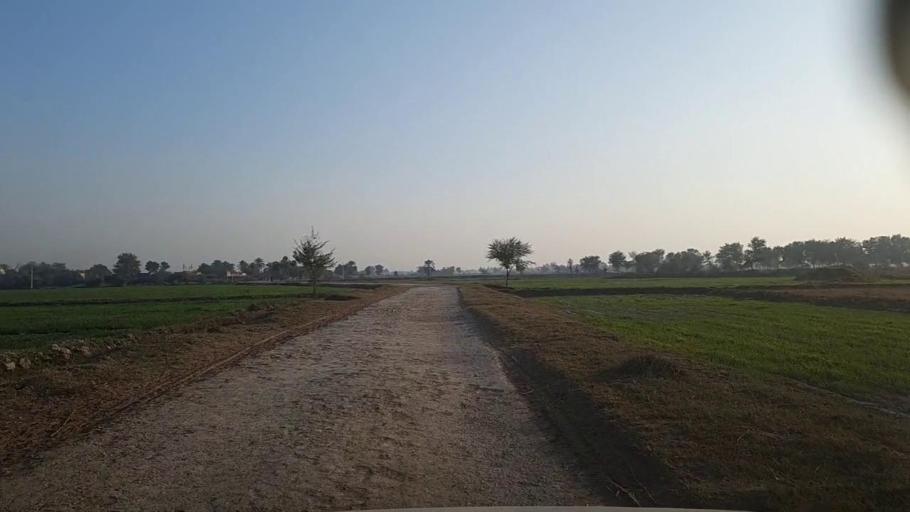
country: PK
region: Sindh
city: Khairpur
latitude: 28.0710
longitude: 69.7500
